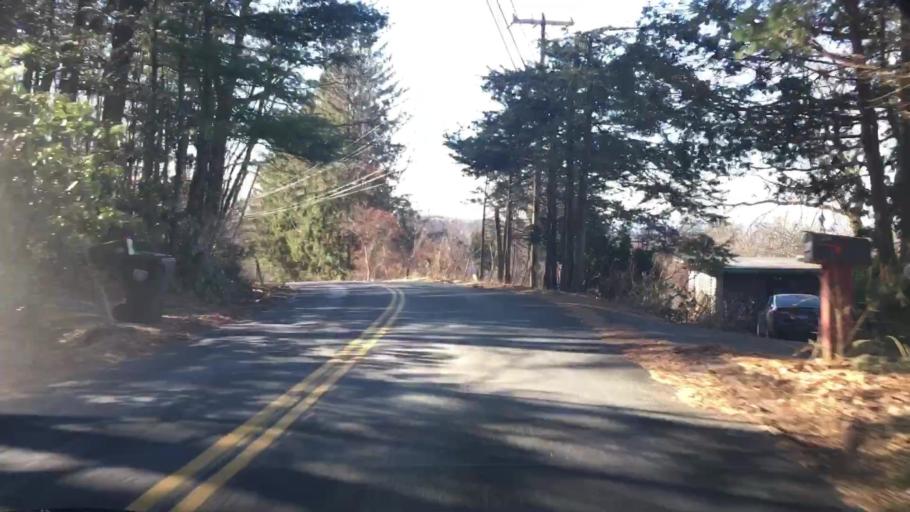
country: US
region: Connecticut
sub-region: Tolland County
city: Somers
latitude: 41.9700
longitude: -72.4239
